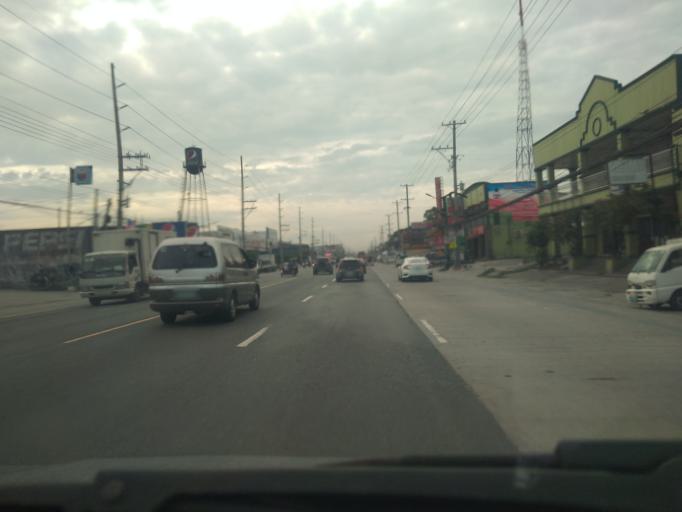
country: PH
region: Central Luzon
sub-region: Province of Pampanga
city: Bulaon
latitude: 15.0702
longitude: 120.6472
